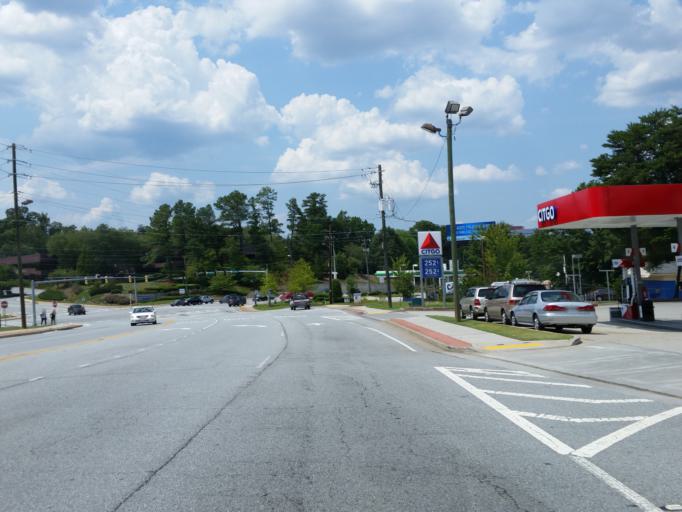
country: US
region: Georgia
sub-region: Fulton County
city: Roswell
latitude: 33.9962
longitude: -84.3498
